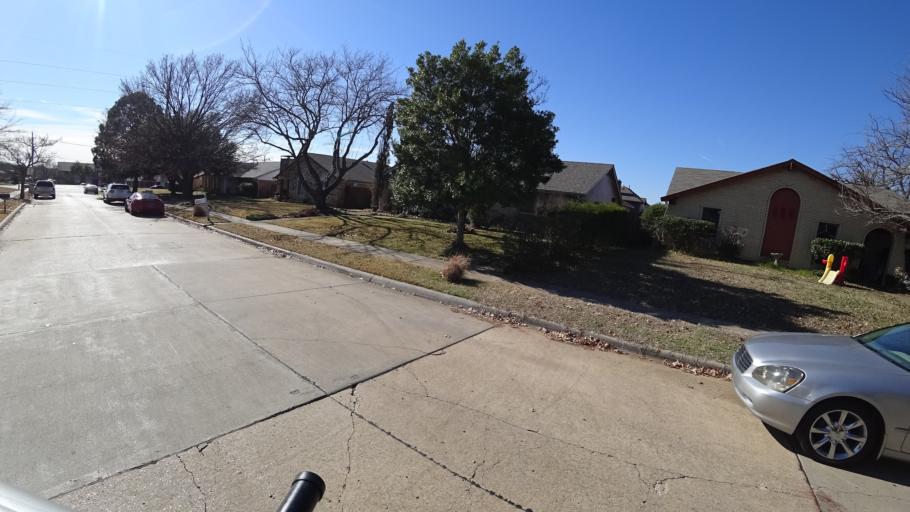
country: US
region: Texas
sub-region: Denton County
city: Lewisville
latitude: 33.0285
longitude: -97.0143
